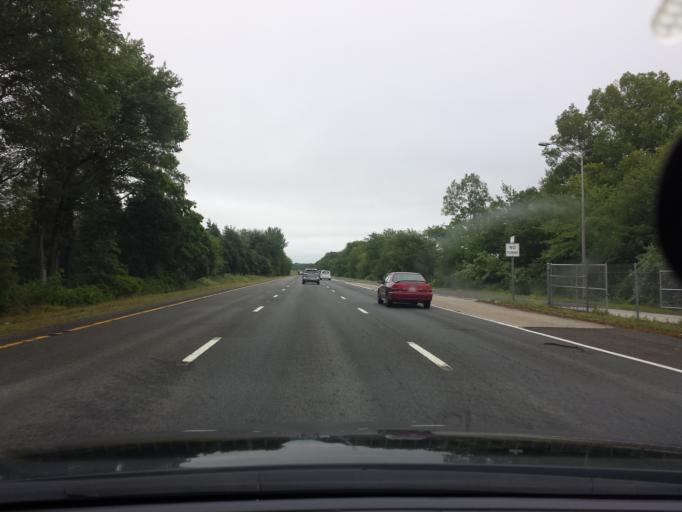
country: US
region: Massachusetts
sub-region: Bristol County
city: Seekonk
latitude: 41.7876
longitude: -71.3003
